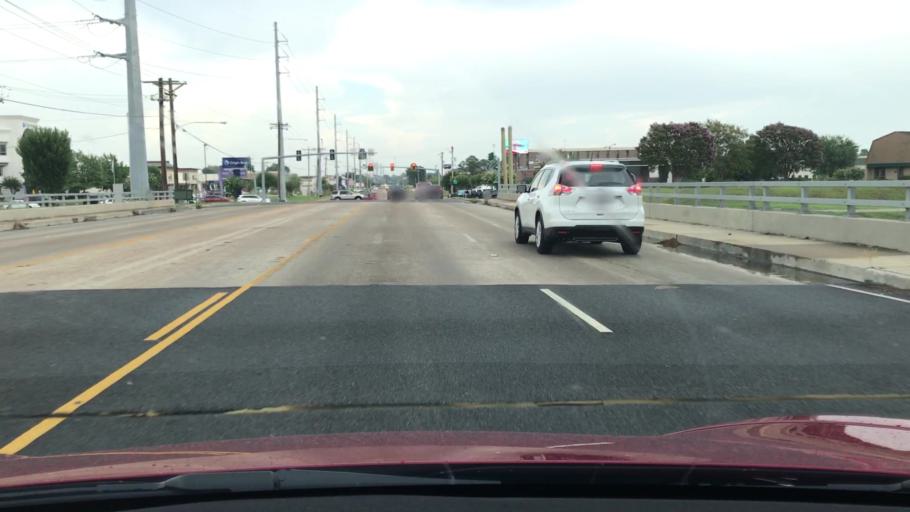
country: US
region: Louisiana
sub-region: Bossier Parish
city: Bossier City
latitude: 32.4434
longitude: -93.7311
